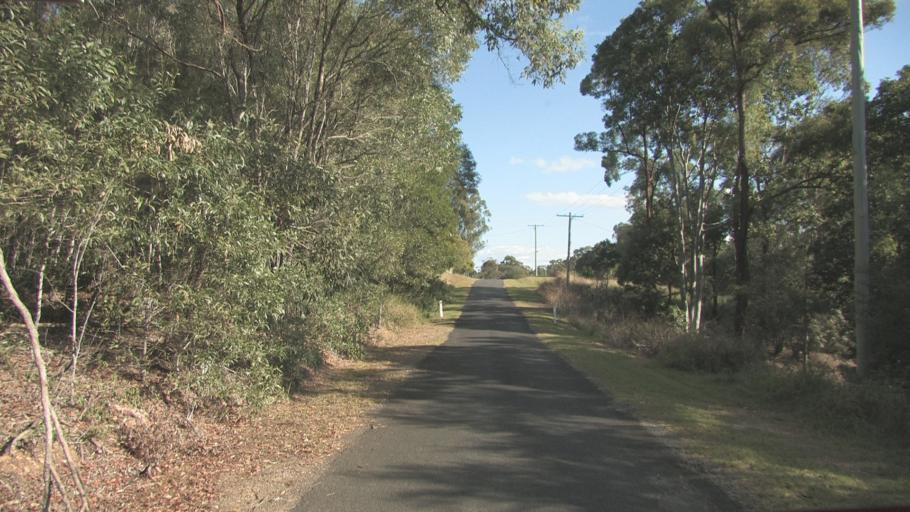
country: AU
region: Queensland
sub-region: Logan
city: Windaroo
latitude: -27.7419
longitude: 153.1627
